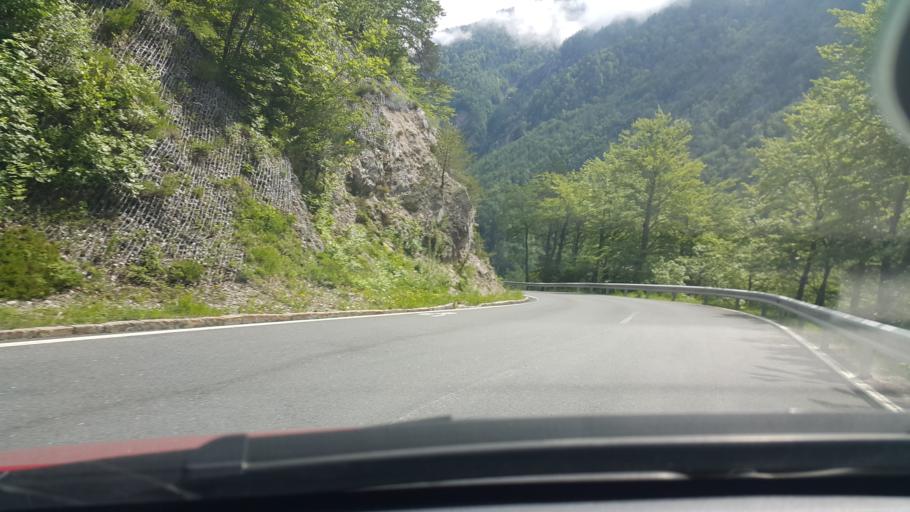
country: AT
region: Carinthia
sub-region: Politischer Bezirk Klagenfurt Land
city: Ferlach
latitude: 46.4908
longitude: 14.2774
